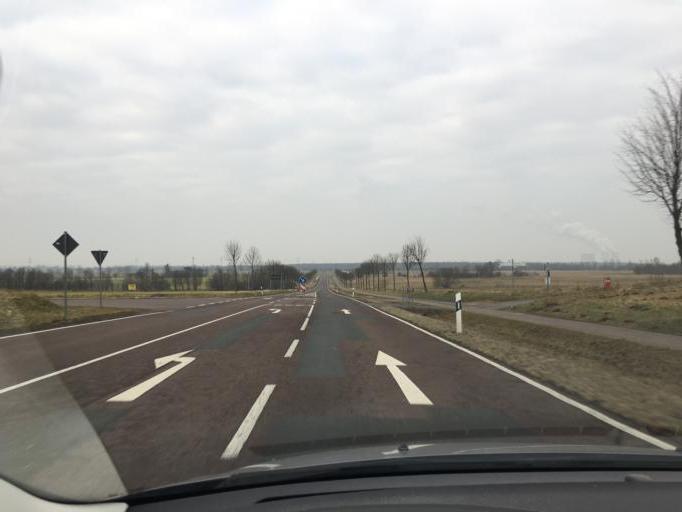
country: DE
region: Saxony
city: Espenhain
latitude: 51.2226
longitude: 12.4616
